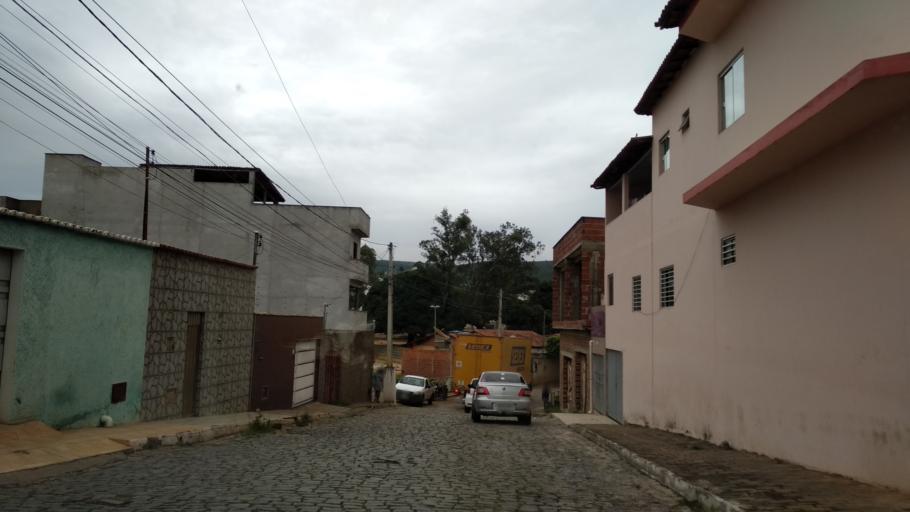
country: BR
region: Bahia
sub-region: Caetite
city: Caetite
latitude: -14.0662
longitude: -42.4802
